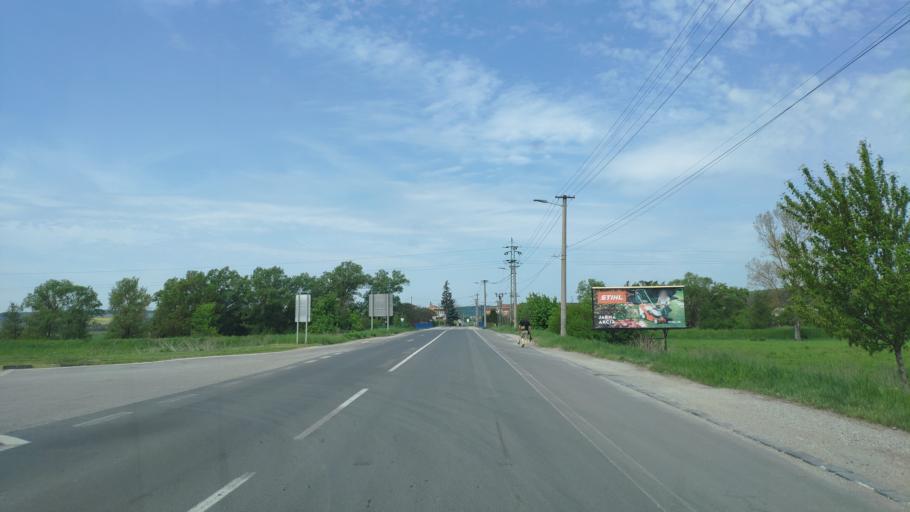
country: HU
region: Borsod-Abauj-Zemplen
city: Putnok
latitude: 48.4236
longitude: 20.3183
